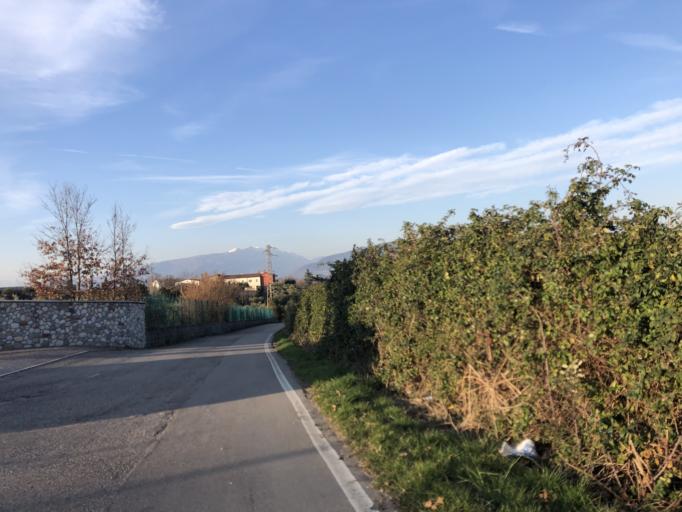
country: IT
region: Veneto
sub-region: Provincia di Verona
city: Pastrengo
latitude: 45.4754
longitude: 10.8191
